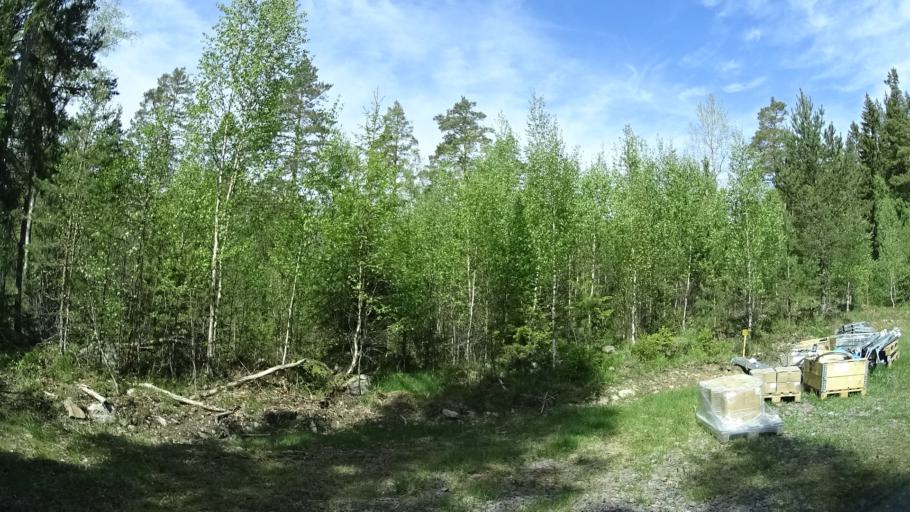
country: SE
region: OEstergoetland
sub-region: Finspangs Kommun
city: Finspang
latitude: 58.8081
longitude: 15.8355
